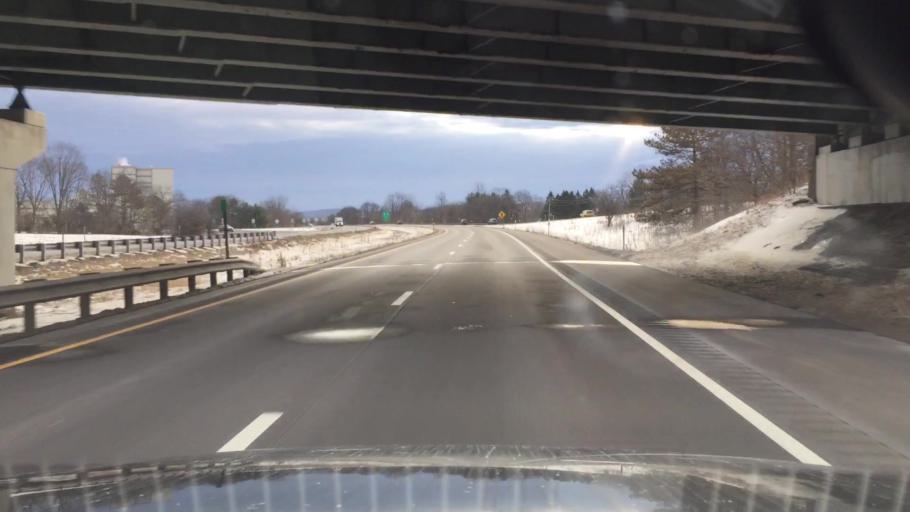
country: US
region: Pennsylvania
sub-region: Bradford County
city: South Waverly
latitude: 41.9992
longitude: -76.5487
